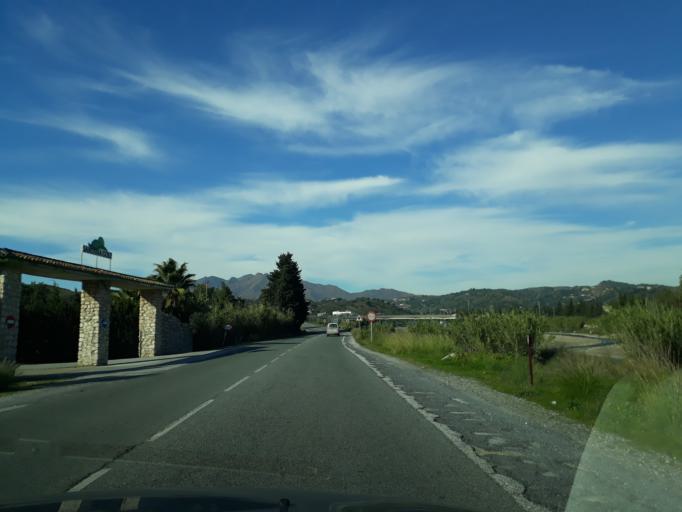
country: ES
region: Andalusia
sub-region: Provincia de Malaga
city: Fuengirola
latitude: 36.5482
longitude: -4.6917
